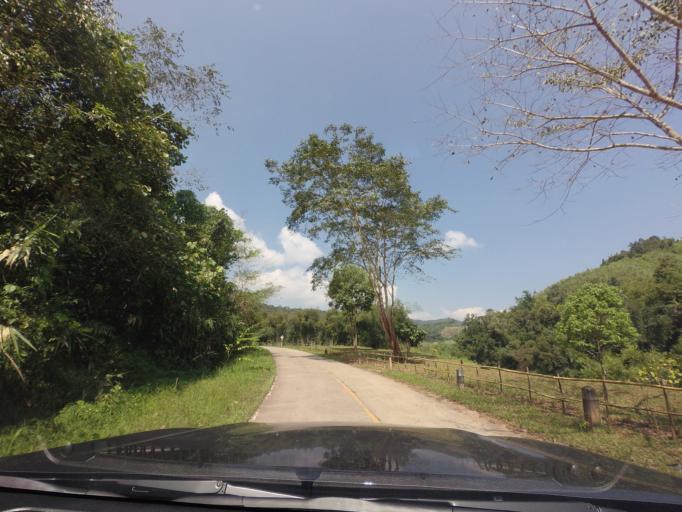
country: TH
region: Nan
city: Bo Kluea
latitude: 19.1972
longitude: 101.1879
